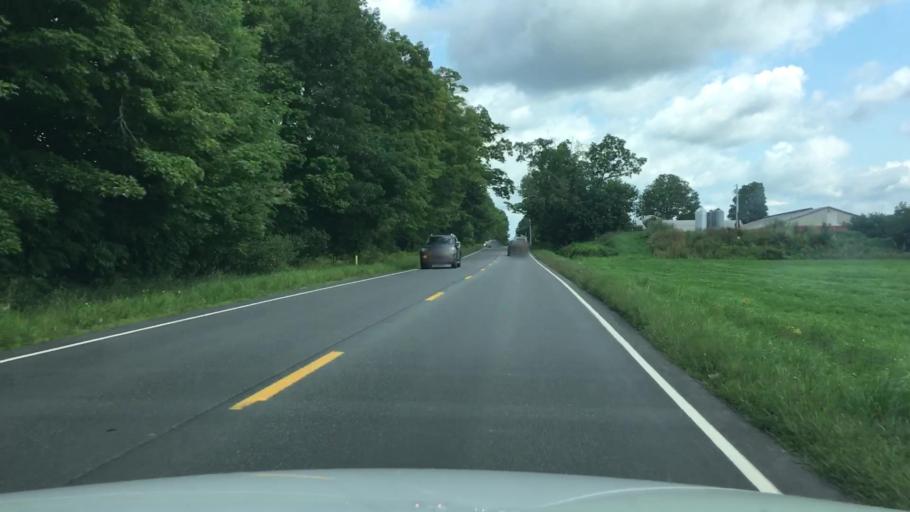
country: US
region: Maine
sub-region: Somerset County
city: Fairfield
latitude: 44.6420
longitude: -69.6780
